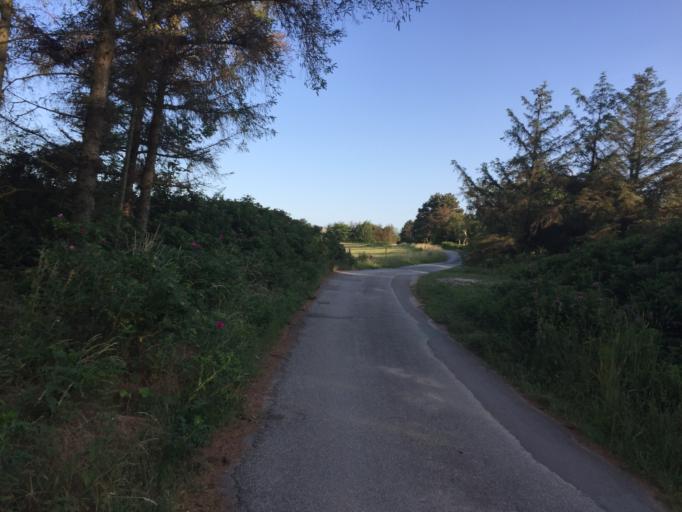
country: DK
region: Zealand
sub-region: Slagelse Kommune
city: Korsor
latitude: 55.2342
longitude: 11.1742
